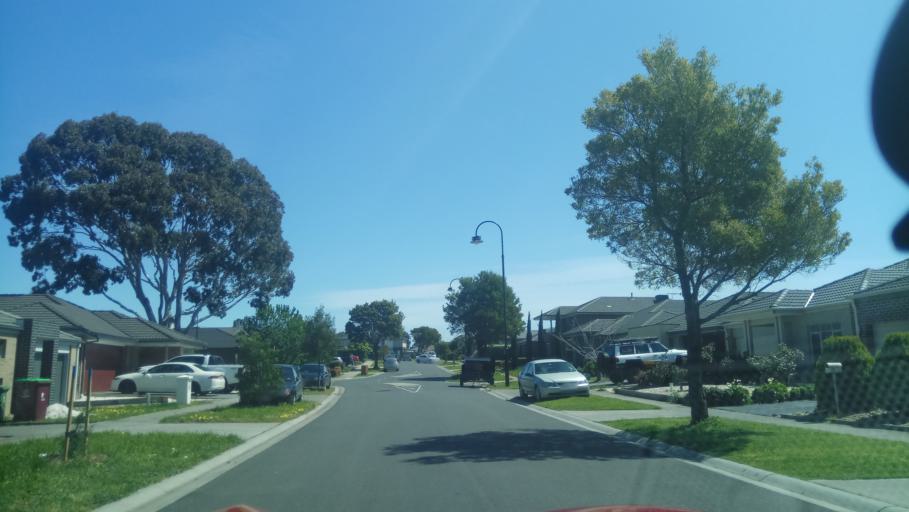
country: AU
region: Victoria
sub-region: Casey
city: Lynbrook
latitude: -38.0636
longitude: 145.2510
